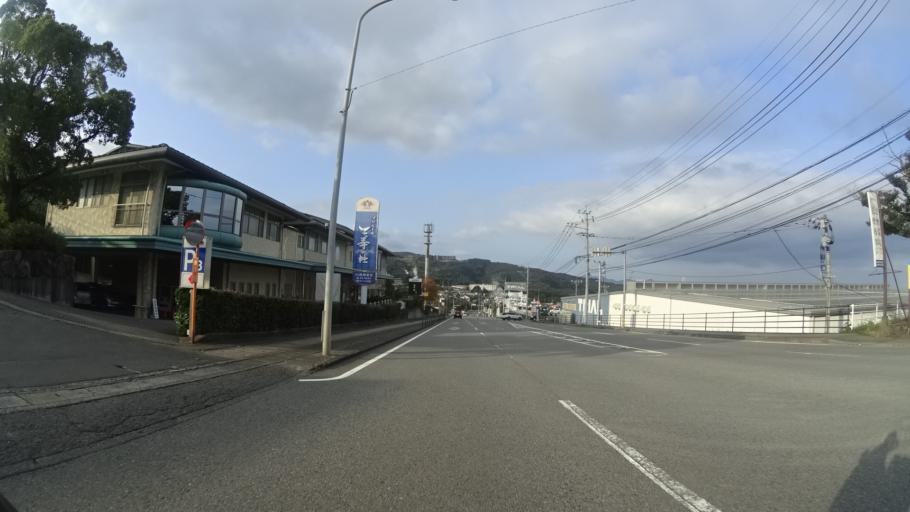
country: JP
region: Oita
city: Beppu
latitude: 33.3030
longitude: 131.4614
